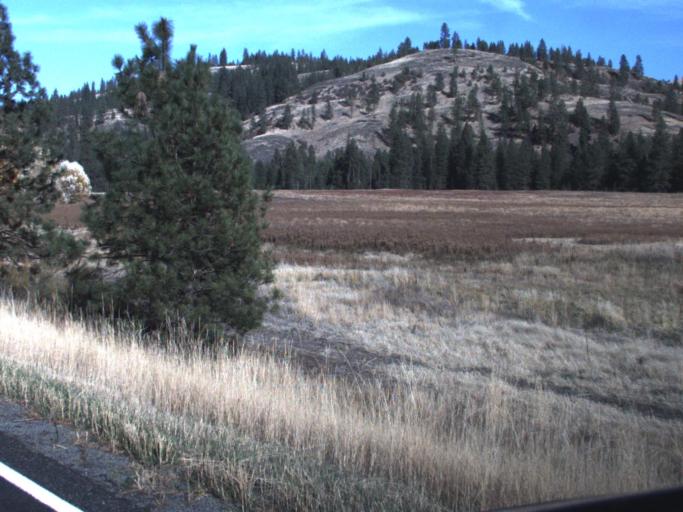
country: US
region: Washington
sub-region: Lincoln County
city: Davenport
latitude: 48.0206
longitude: -118.2363
